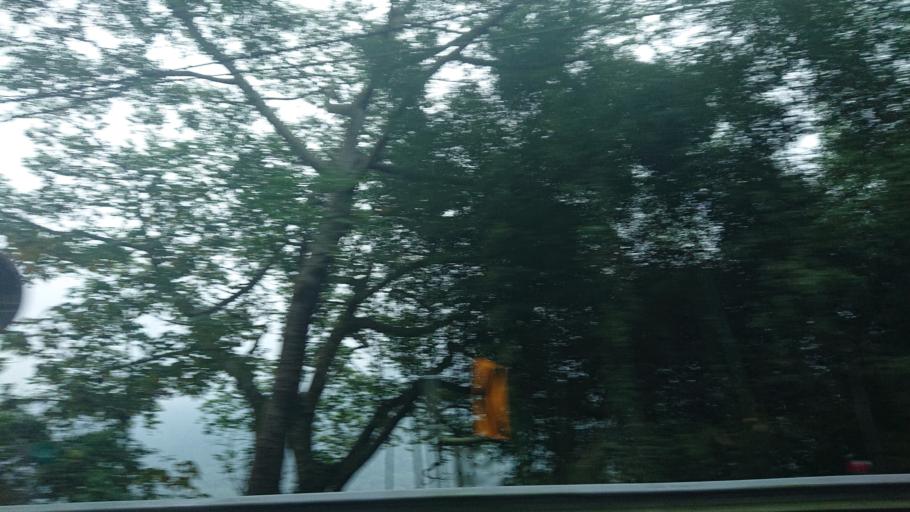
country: TW
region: Taiwan
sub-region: Chiayi
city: Jiayi Shi
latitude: 23.4702
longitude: 120.7102
